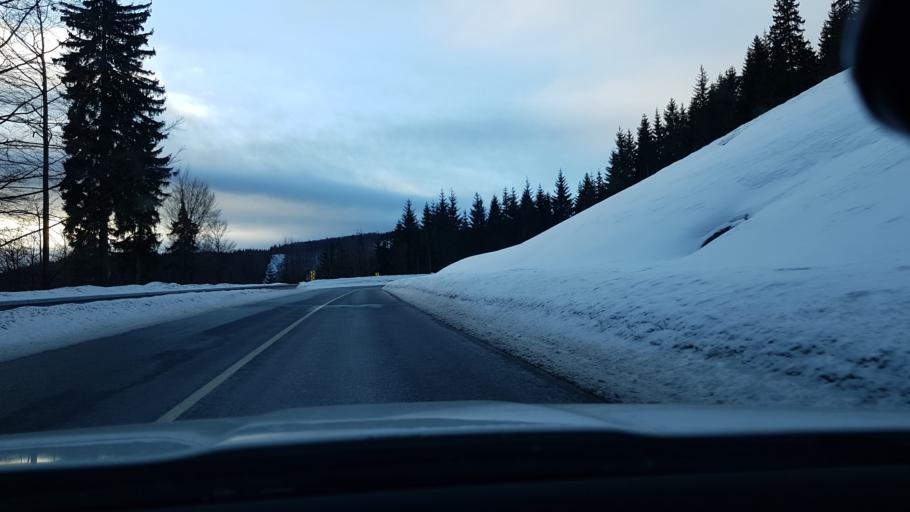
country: CZ
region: Olomoucky
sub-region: Okres Sumperk
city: Loucna nad Desnou
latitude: 50.1142
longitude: 17.1469
